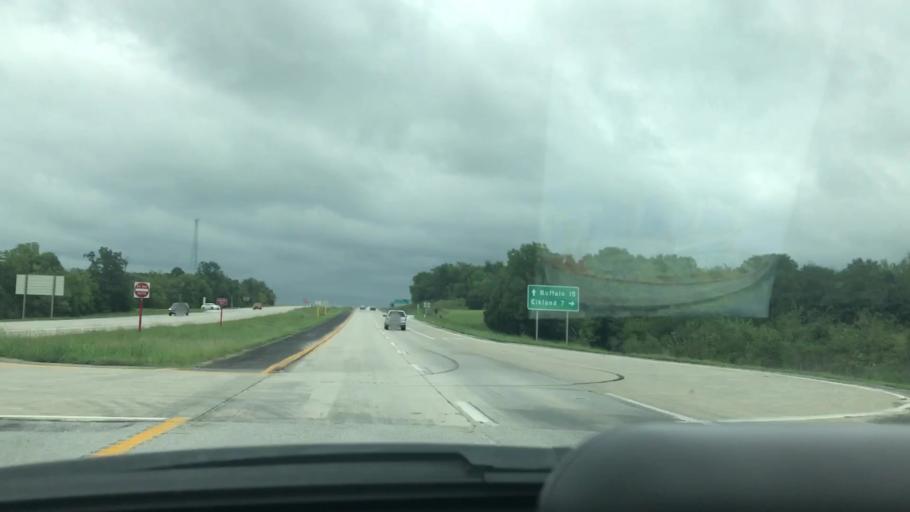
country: US
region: Missouri
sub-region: Greene County
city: Fair Grove
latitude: 37.4208
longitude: -93.1451
